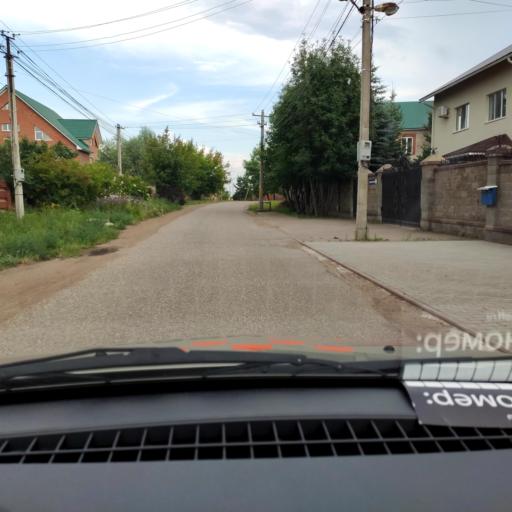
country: RU
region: Bashkortostan
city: Ufa
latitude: 54.6199
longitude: 55.9177
